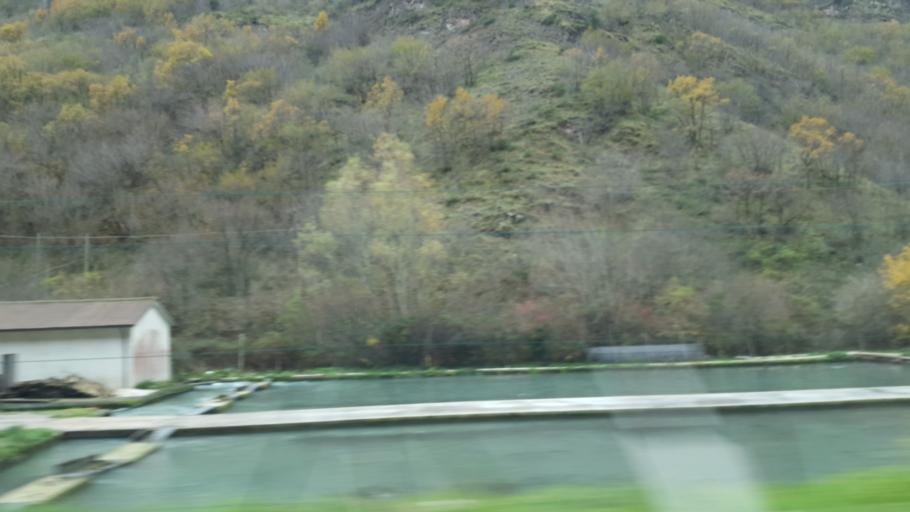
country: IT
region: The Marches
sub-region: Provincia di Macerata
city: Visso
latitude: 42.9243
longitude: 13.1037
